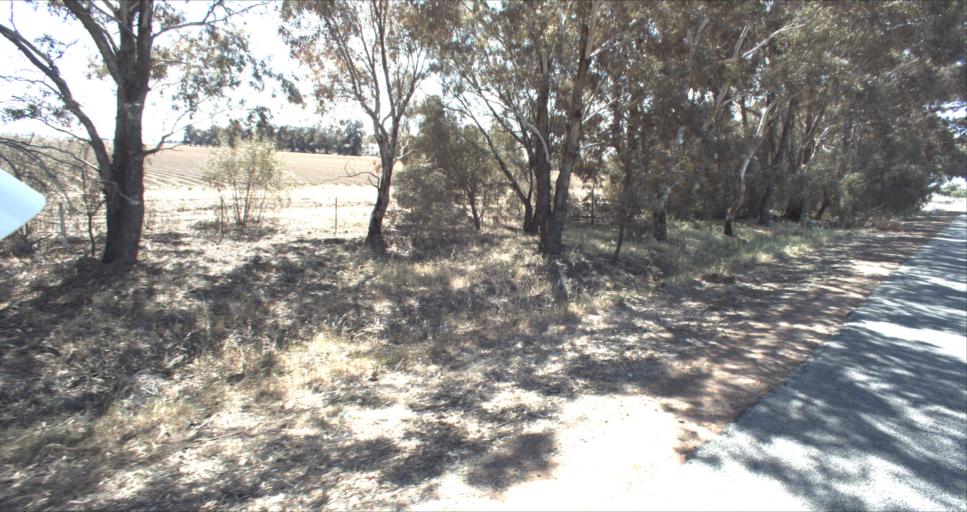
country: AU
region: New South Wales
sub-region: Leeton
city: Leeton
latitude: -34.5797
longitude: 146.2792
